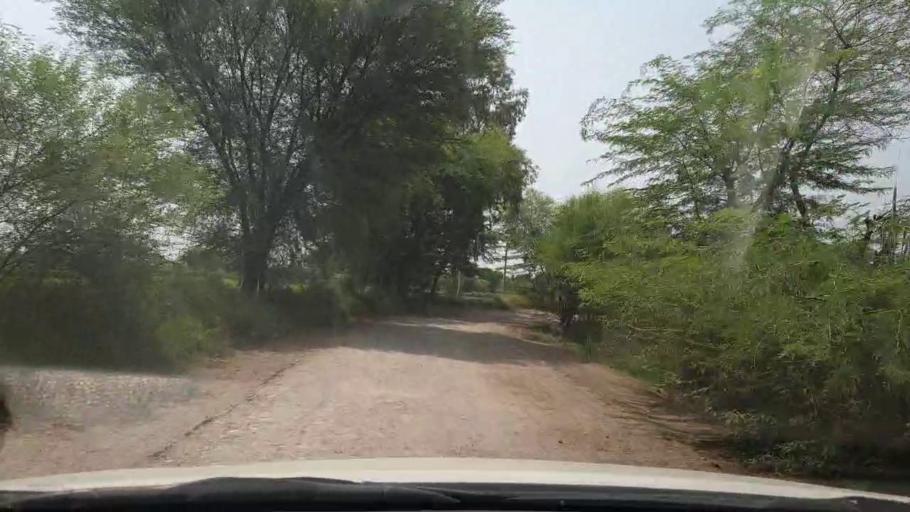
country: PK
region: Sindh
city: Rustam jo Goth
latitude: 27.9796
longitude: 68.7226
